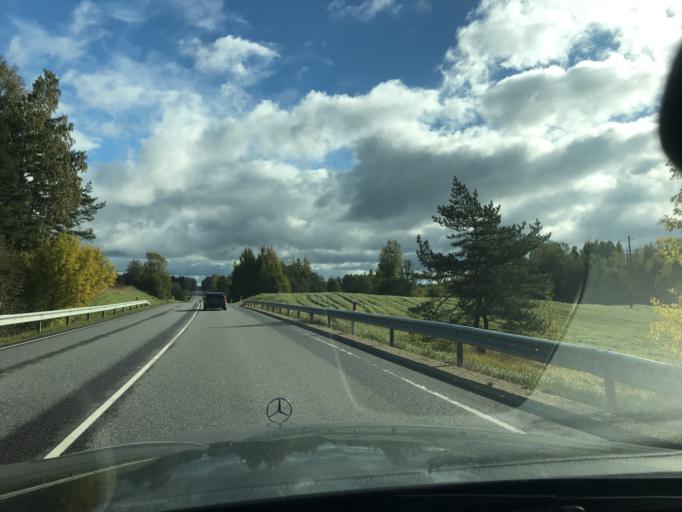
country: EE
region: Vorumaa
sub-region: Voru linn
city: Voru
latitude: 57.7812
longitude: 27.1081
